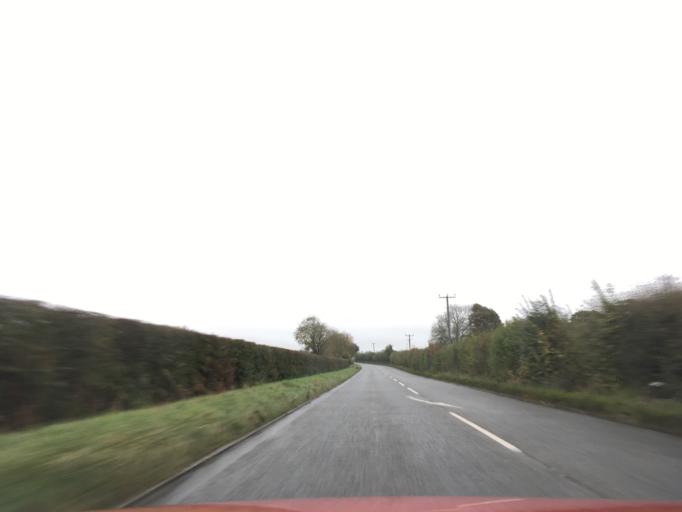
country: GB
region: England
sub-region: West Berkshire
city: Wickham
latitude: 51.4533
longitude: -1.4641
